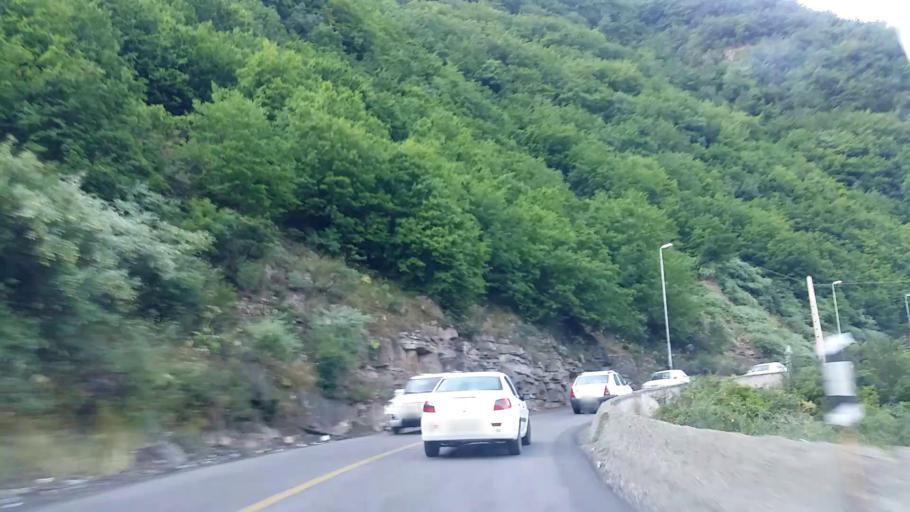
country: IR
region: Mazandaran
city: Chalus
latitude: 36.2305
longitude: 51.3136
